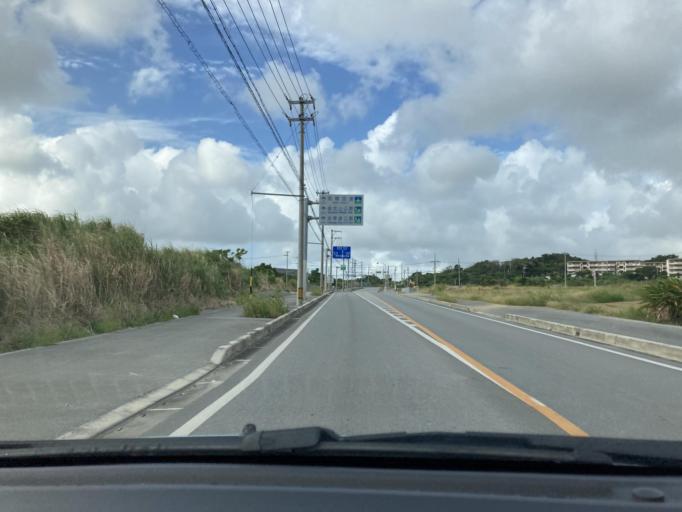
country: JP
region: Okinawa
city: Itoman
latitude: 26.1164
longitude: 127.6919
